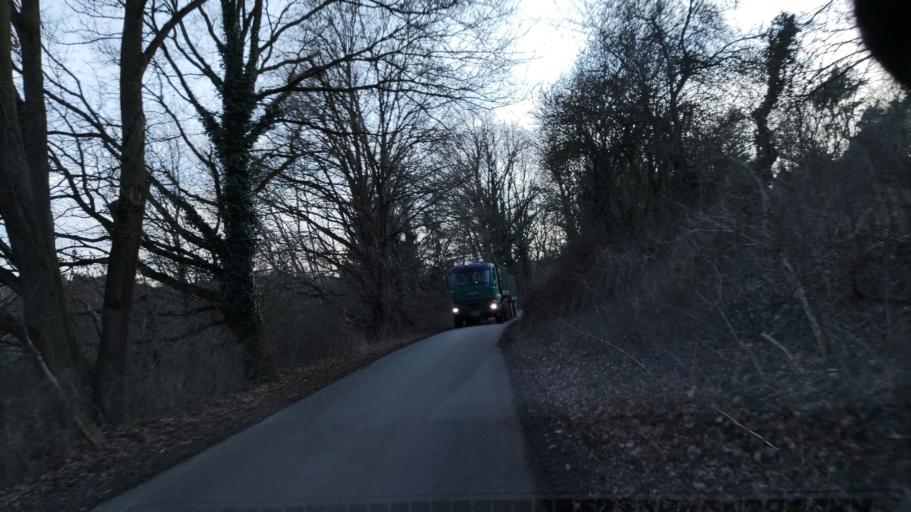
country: DE
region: Lower Saxony
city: Thomasburg
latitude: 53.2078
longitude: 10.6966
